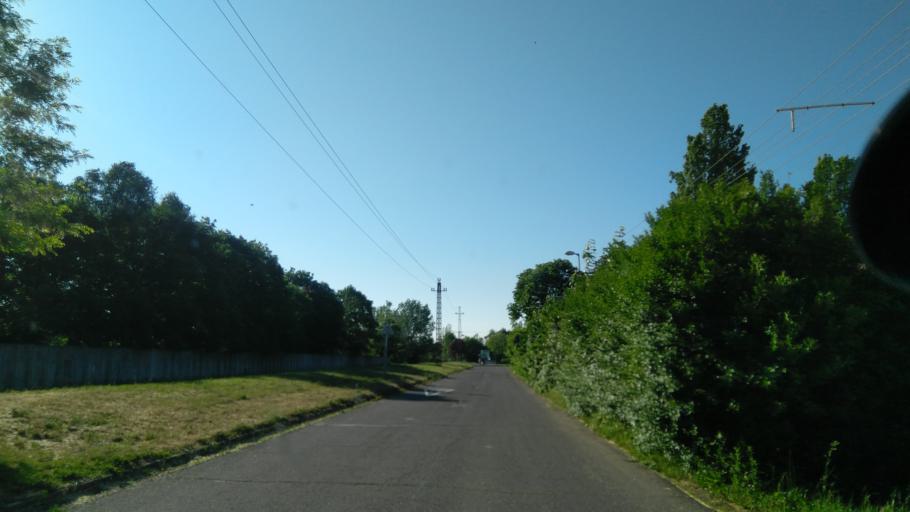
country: HU
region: Bekes
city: Gyula
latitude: 46.6368
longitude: 21.2577
